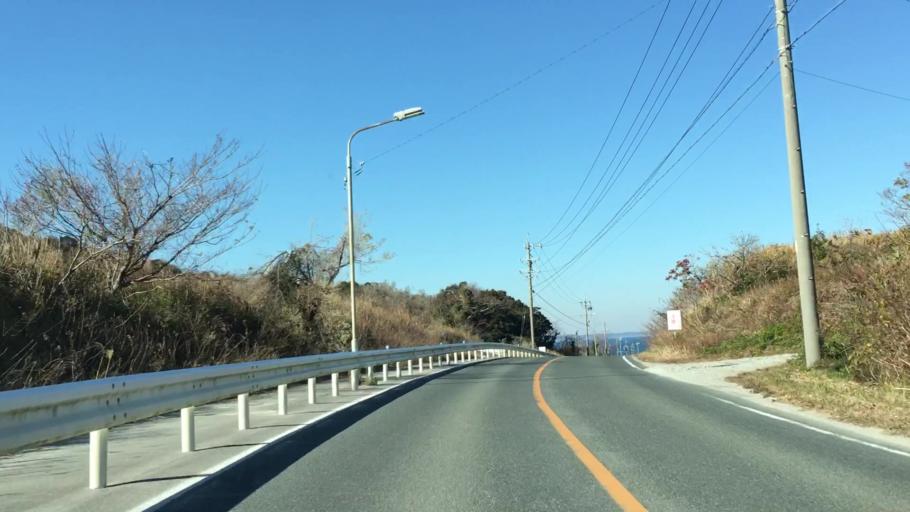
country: JP
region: Aichi
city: Tahara
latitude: 34.6839
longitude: 137.2492
